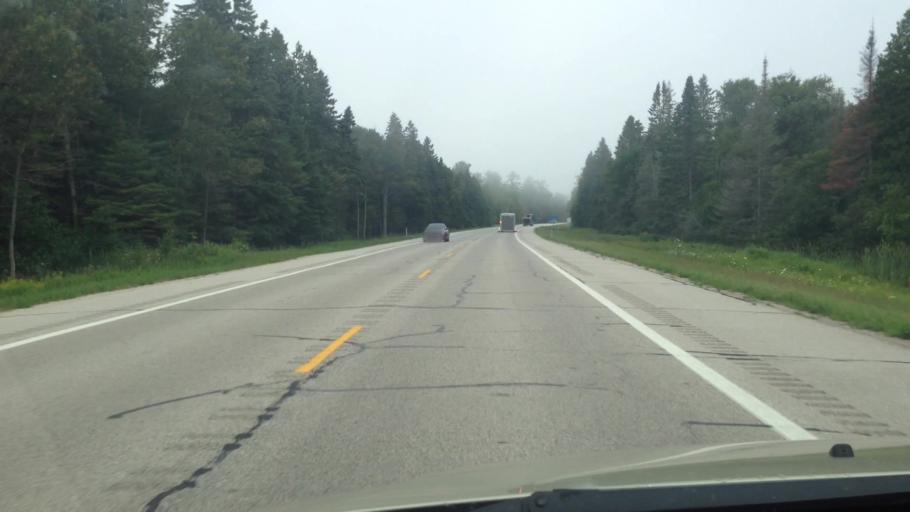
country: US
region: Michigan
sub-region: Luce County
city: Newberry
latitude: 46.0944
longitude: -85.3836
